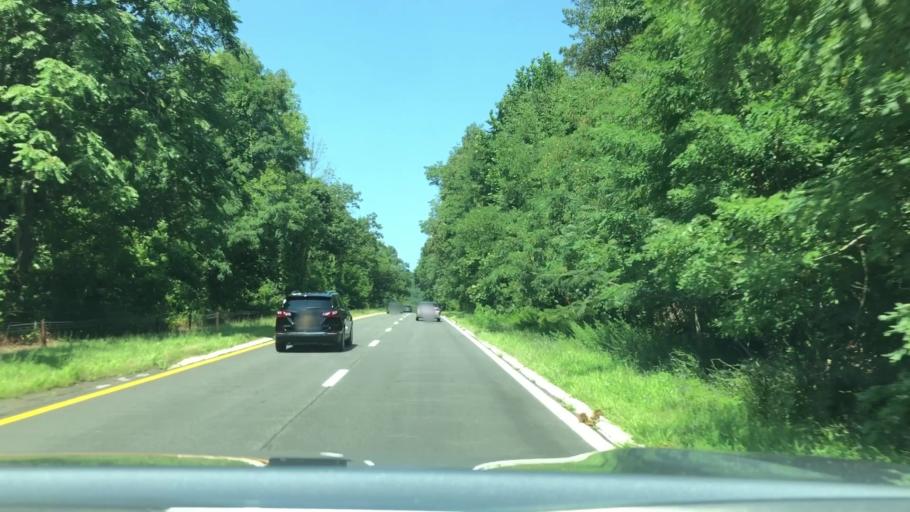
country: US
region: New York
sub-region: Rockland County
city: Thiells
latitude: 41.2470
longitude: -74.0326
